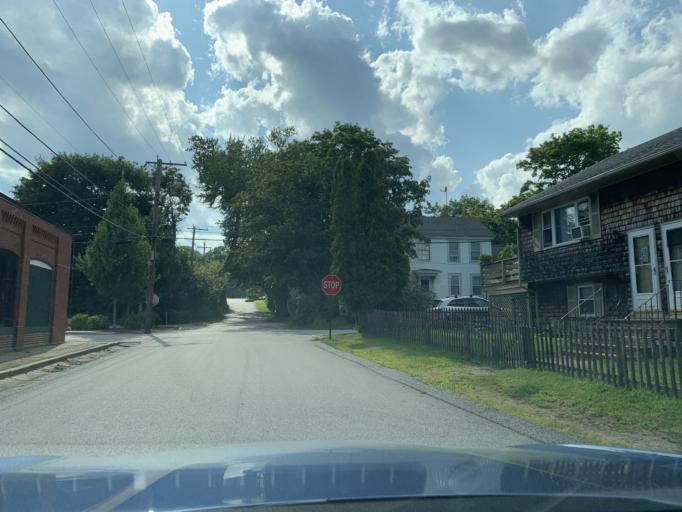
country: US
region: Rhode Island
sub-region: Kent County
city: East Greenwich
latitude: 41.6652
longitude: -71.4480
